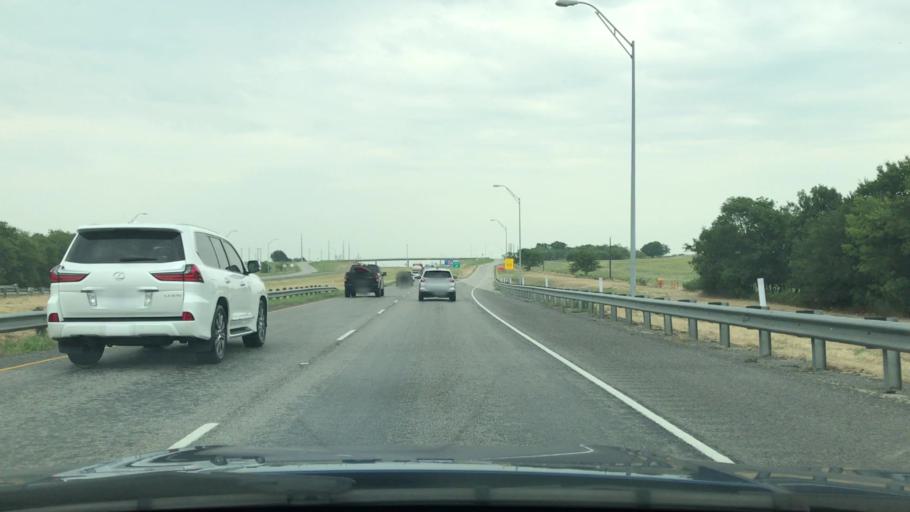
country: US
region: Texas
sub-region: Kaufman County
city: Talty
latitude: 32.7329
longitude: -96.3469
